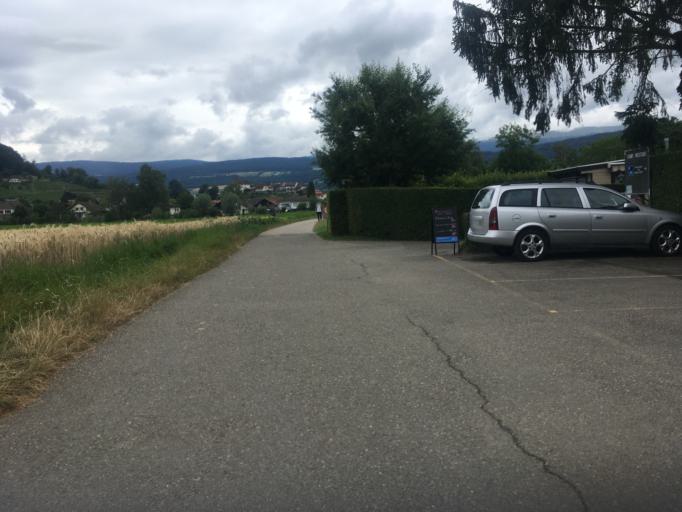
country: CH
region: Bern
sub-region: Seeland District
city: Erlach
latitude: 47.0390
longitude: 7.1036
